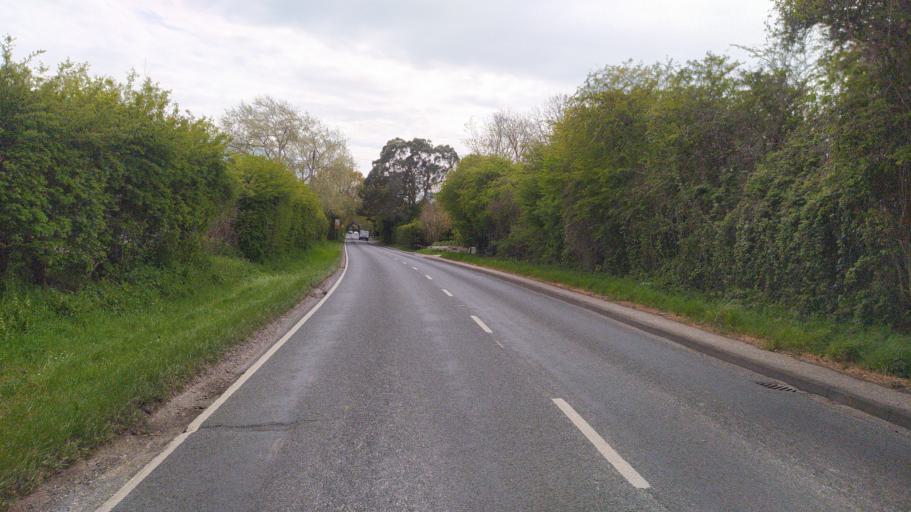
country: GB
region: England
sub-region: West Sussex
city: Birdham
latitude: 50.7830
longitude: -0.8417
